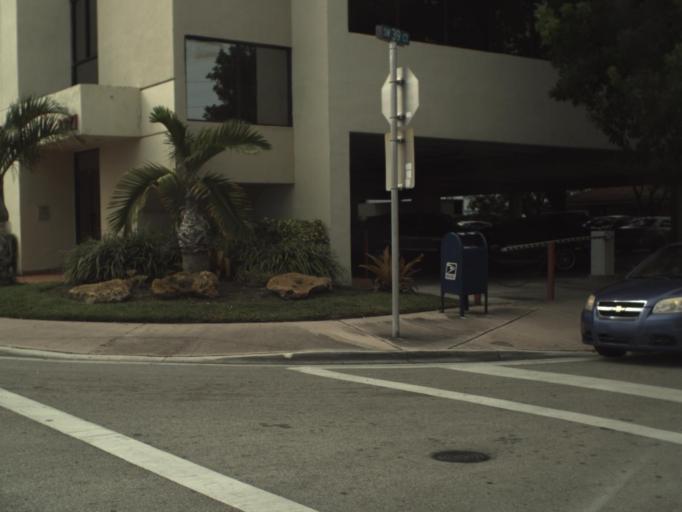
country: US
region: Florida
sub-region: Miami-Dade County
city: West Miami
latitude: 25.7646
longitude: -80.2608
